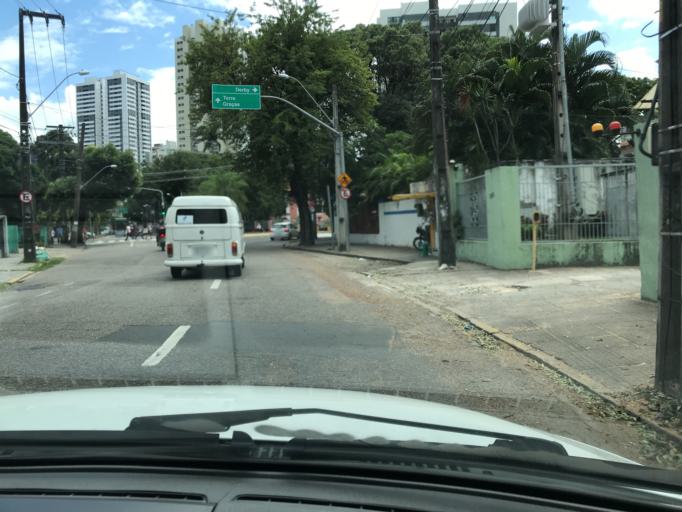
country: BR
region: Pernambuco
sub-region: Recife
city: Recife
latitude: -8.0594
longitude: -34.9019
